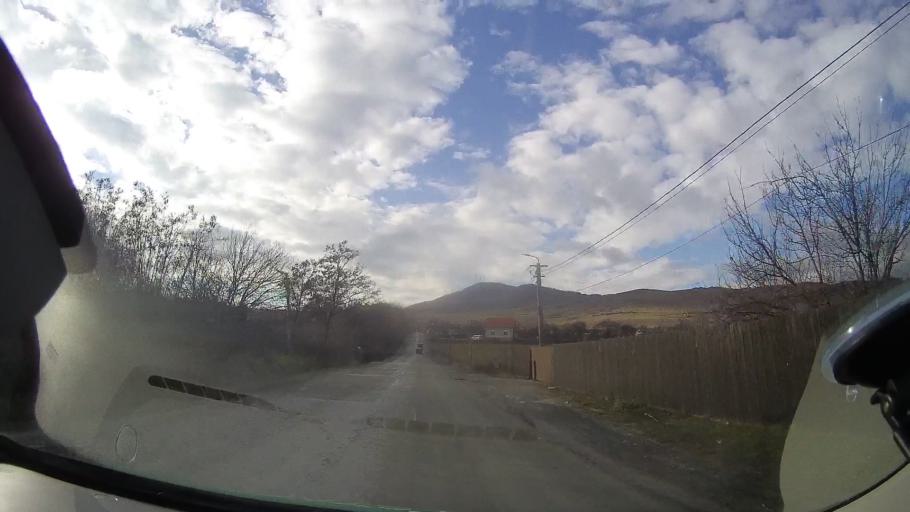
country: RO
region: Cluj
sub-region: Comuna Baisoara
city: Baisoara
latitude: 46.6221
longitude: 23.4505
